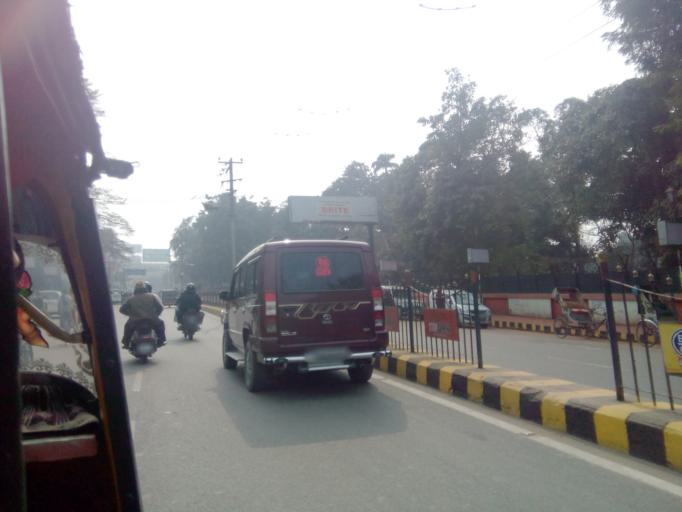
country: IN
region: Bihar
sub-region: Patna
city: Patna
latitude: 25.6154
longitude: 85.1417
